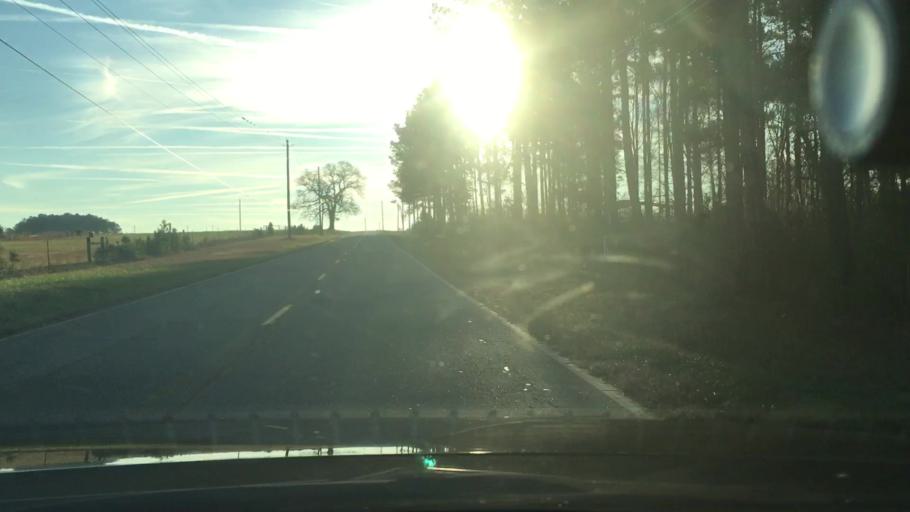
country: US
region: Georgia
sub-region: Spalding County
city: Experiment
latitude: 33.2651
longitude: -84.3087
